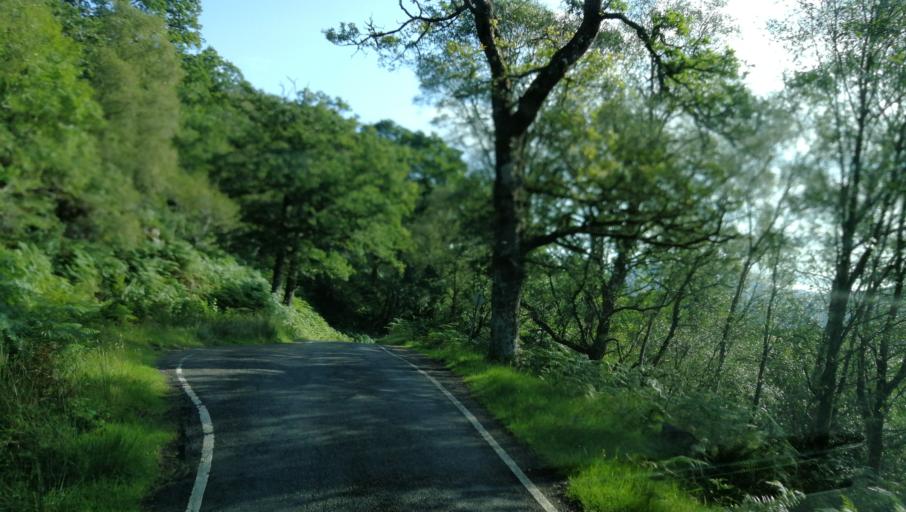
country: GB
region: Scotland
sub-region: Argyll and Bute
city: Isle Of Mull
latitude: 56.6791
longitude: -5.8350
